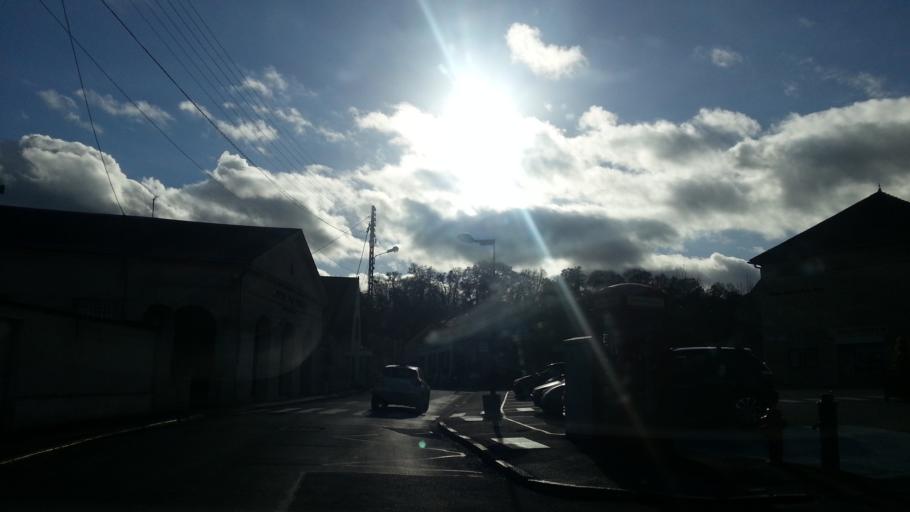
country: FR
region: Picardie
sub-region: Departement de l'Oise
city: Verneuil-en-Halatte
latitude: 49.2746
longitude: 2.5174
